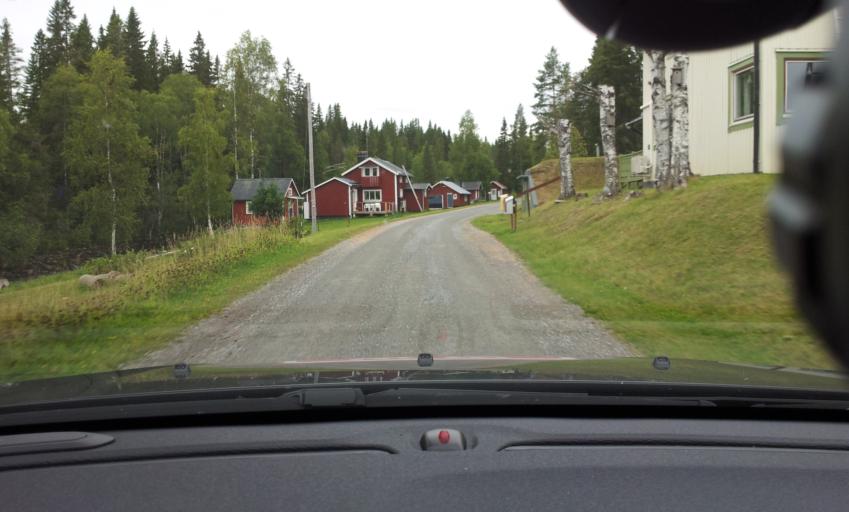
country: SE
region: Jaemtland
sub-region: OEstersunds Kommun
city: Brunflo
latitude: 62.9930
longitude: 14.9730
